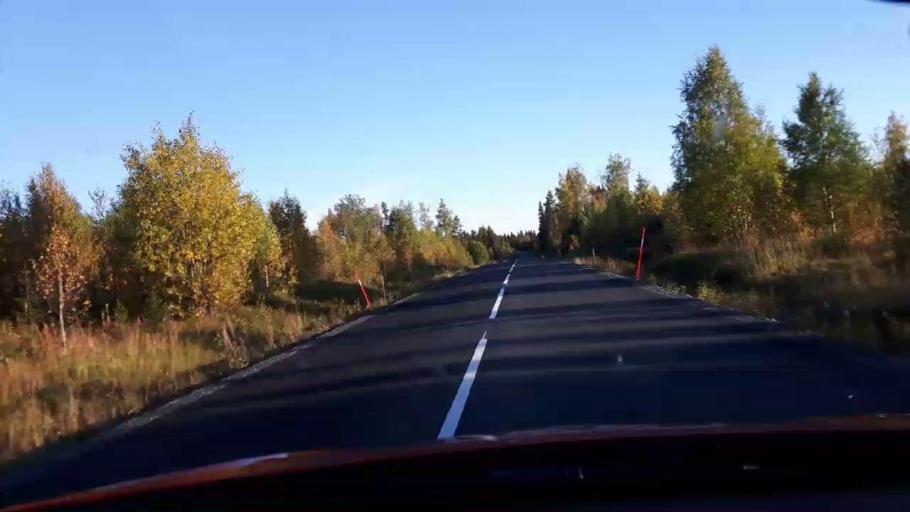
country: SE
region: Jaemtland
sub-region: OEstersunds Kommun
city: Lit
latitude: 63.4928
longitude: 14.8766
